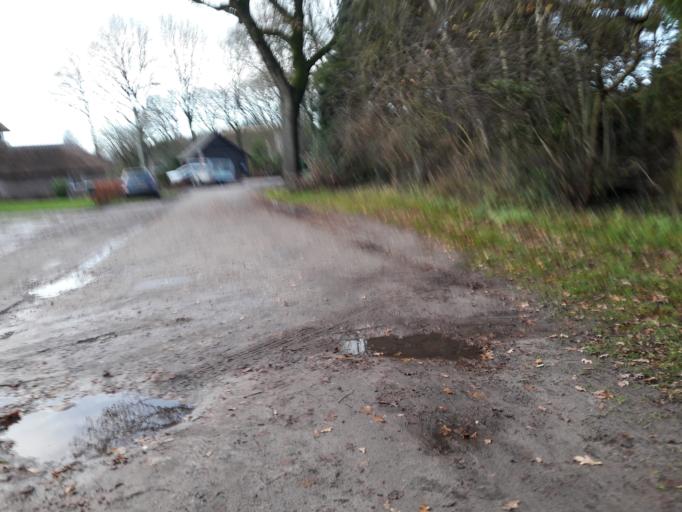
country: NL
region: Drenthe
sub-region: Gemeente Borger-Odoorn
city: Borger
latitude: 52.9543
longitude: 6.7973
